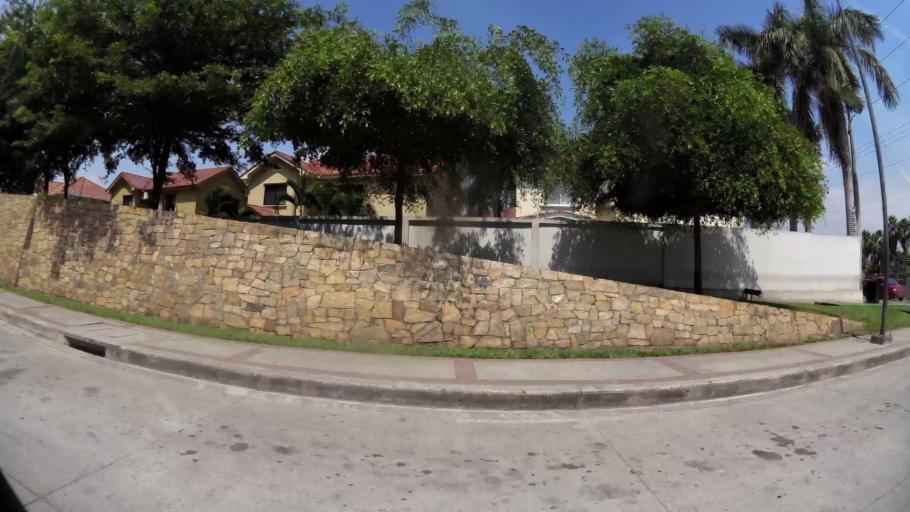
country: EC
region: Guayas
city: Eloy Alfaro
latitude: -2.1038
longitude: -79.8728
